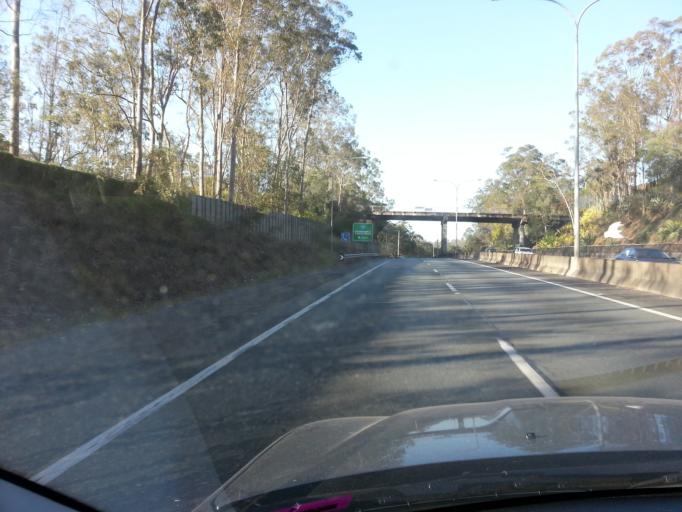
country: AU
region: Queensland
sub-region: Brisbane
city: Kenmore Hills
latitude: -27.5123
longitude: 152.9577
